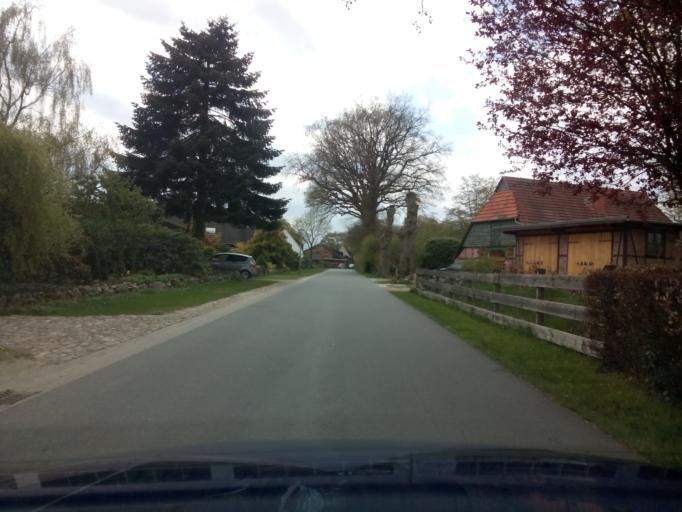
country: DE
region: Lower Saxony
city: Vollersode
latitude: 53.3189
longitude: 8.8829
